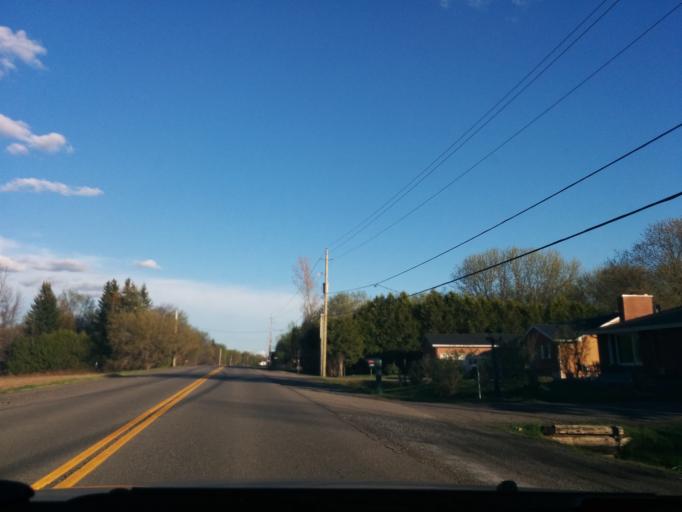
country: CA
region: Ontario
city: Ottawa
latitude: 45.2077
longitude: -75.6458
